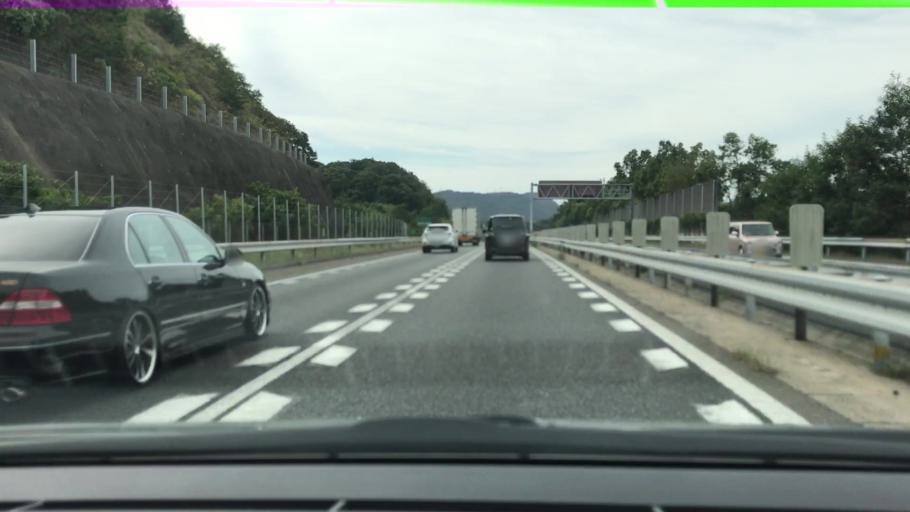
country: JP
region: Hyogo
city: Aioi
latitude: 34.8156
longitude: 134.4577
